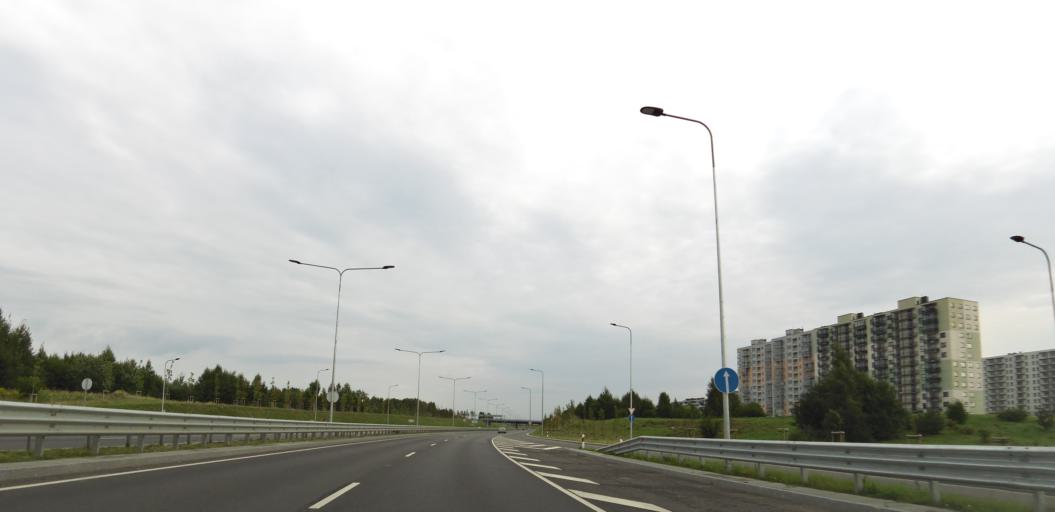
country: LT
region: Vilnius County
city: Pasilaiciai
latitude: 54.7365
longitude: 25.2092
